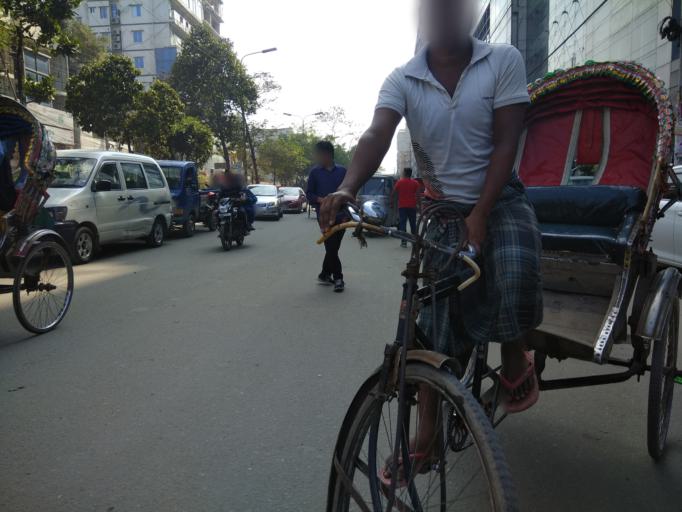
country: BD
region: Dhaka
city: Azimpur
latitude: 23.7653
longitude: 90.3586
